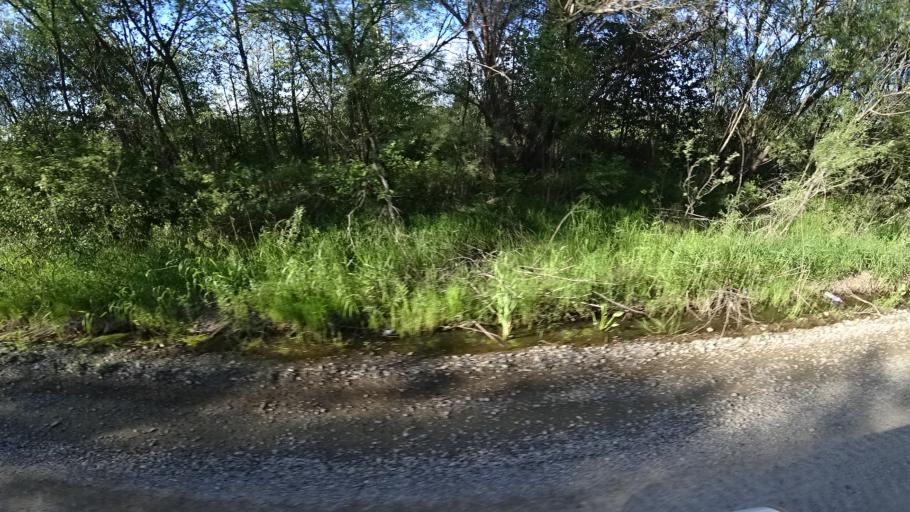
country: RU
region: Khabarovsk Krai
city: Khor
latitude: 47.8426
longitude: 134.9543
